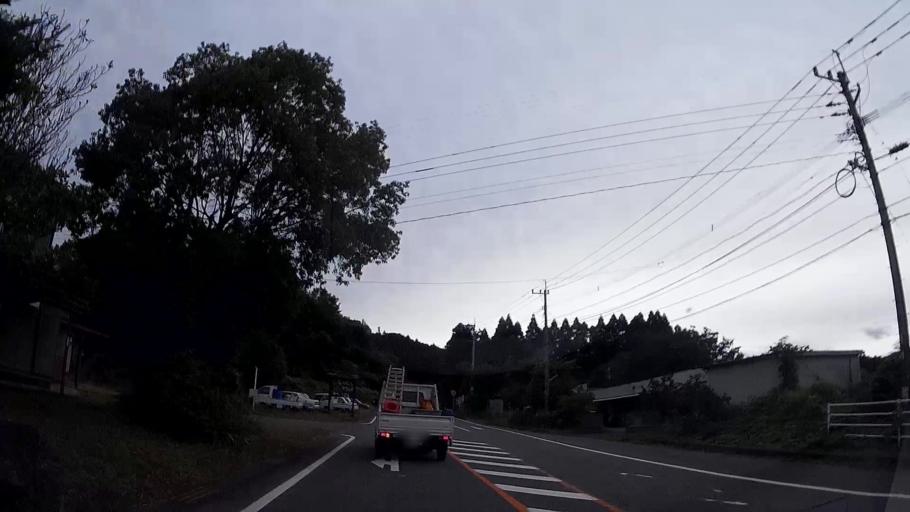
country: JP
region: Kumamoto
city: Kikuchi
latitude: 33.0158
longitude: 130.8644
